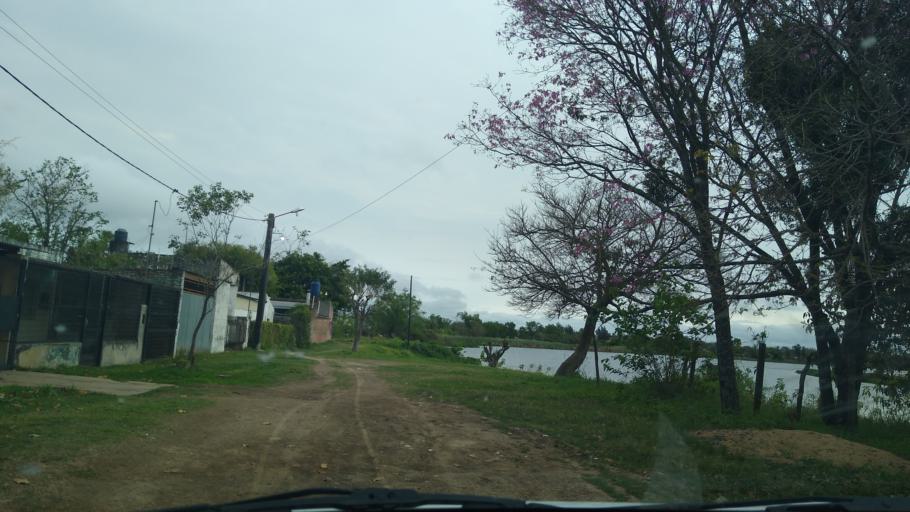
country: AR
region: Chaco
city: Barranqueras
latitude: -27.4814
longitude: -58.9420
